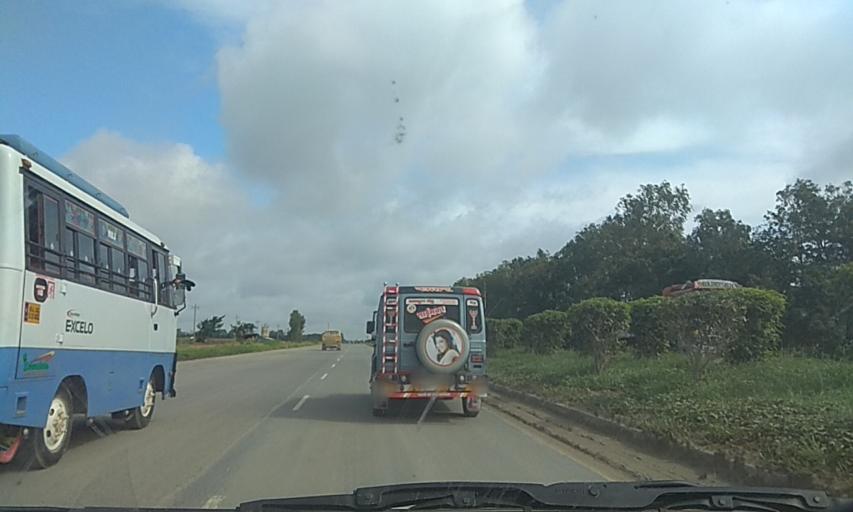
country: IN
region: Karnataka
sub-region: Haveri
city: Shiggaon
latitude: 15.0453
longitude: 75.1705
